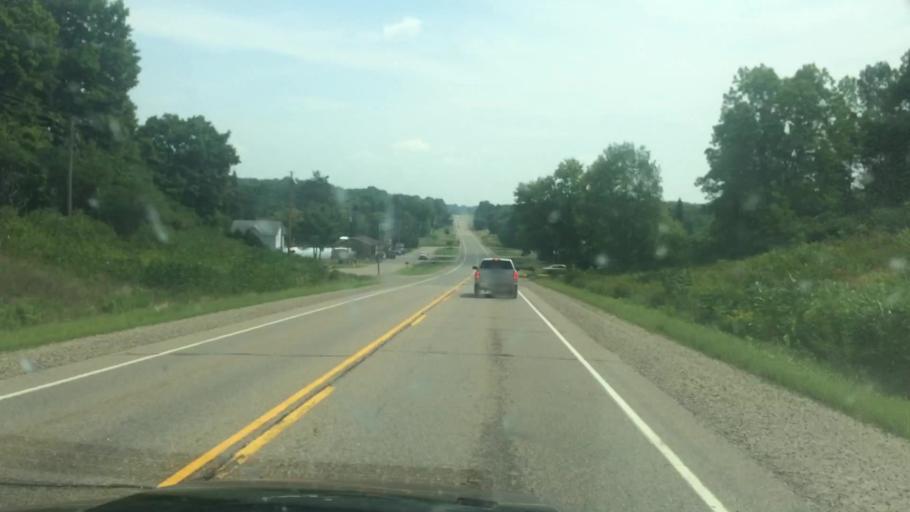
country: US
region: Wisconsin
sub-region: Langlade County
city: Antigo
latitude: 45.1682
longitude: -88.8900
